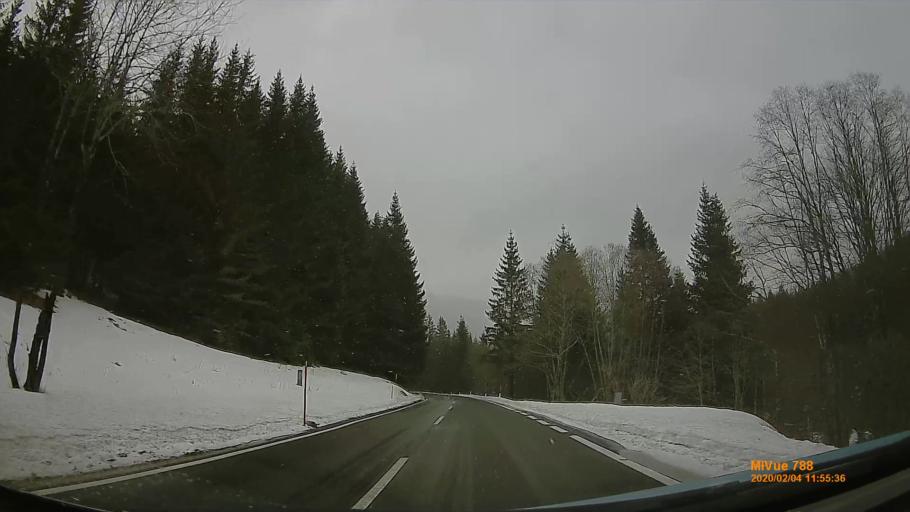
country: AT
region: Styria
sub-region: Politischer Bezirk Bruck-Muerzzuschlag
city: Muerzsteg
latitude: 47.7556
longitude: 15.5126
